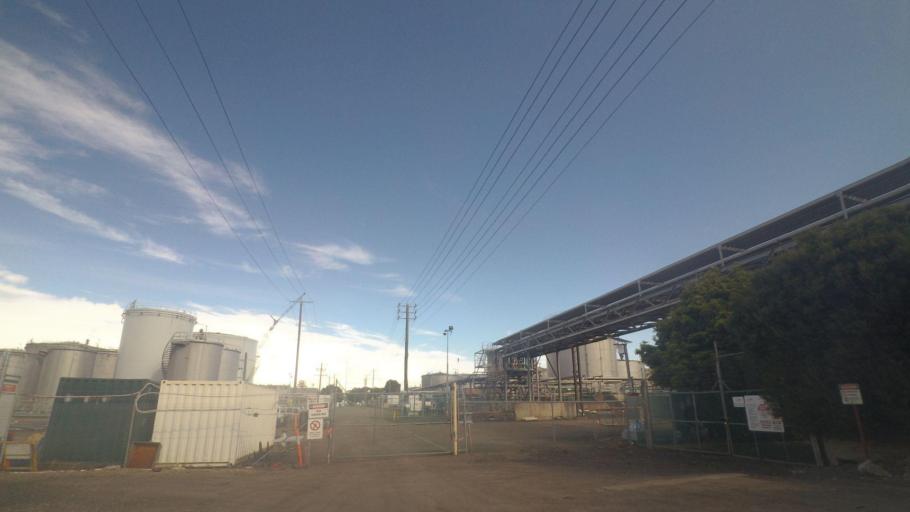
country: AU
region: Victoria
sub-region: Hobsons Bay
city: Spotswood
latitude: -37.8372
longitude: 144.8887
